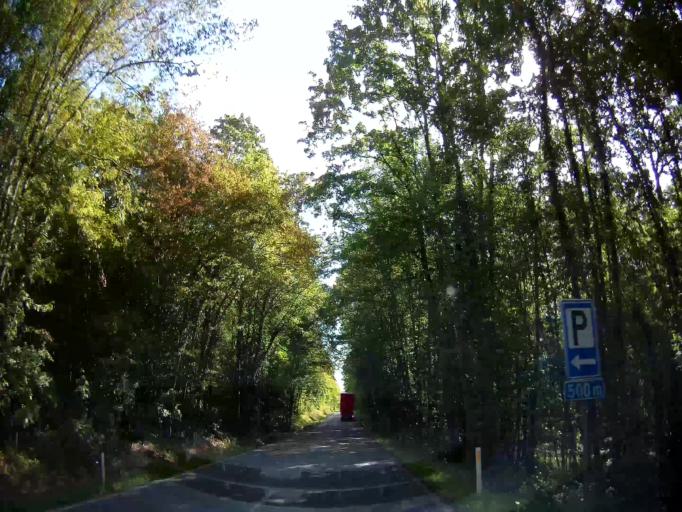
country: BE
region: Wallonia
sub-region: Province de Namur
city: Rochefort
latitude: 50.1675
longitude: 5.1664
